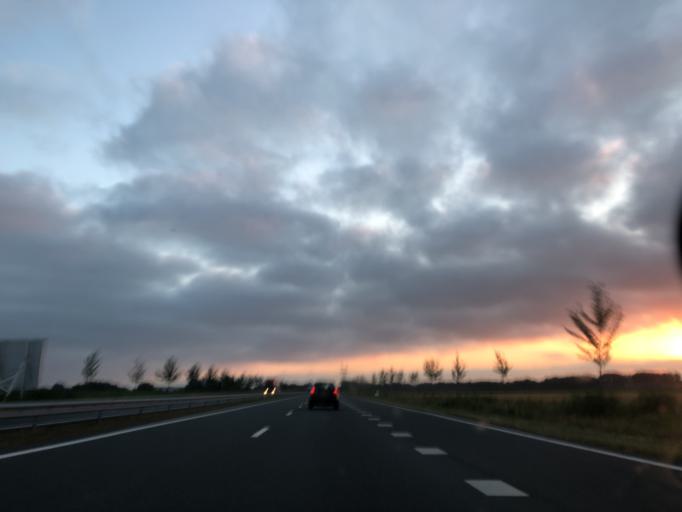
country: NL
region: Groningen
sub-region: Gemeente Veendam
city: Veendam
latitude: 53.0804
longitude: 6.8840
